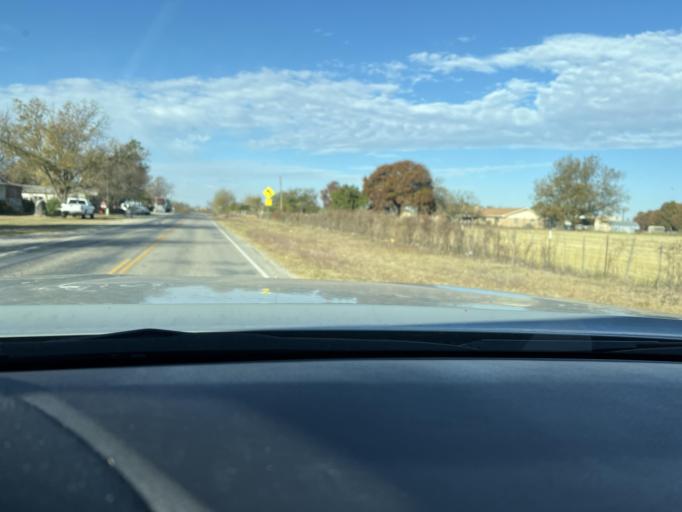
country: US
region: Texas
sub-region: Eastland County
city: Eastland
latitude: 32.4193
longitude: -98.7543
